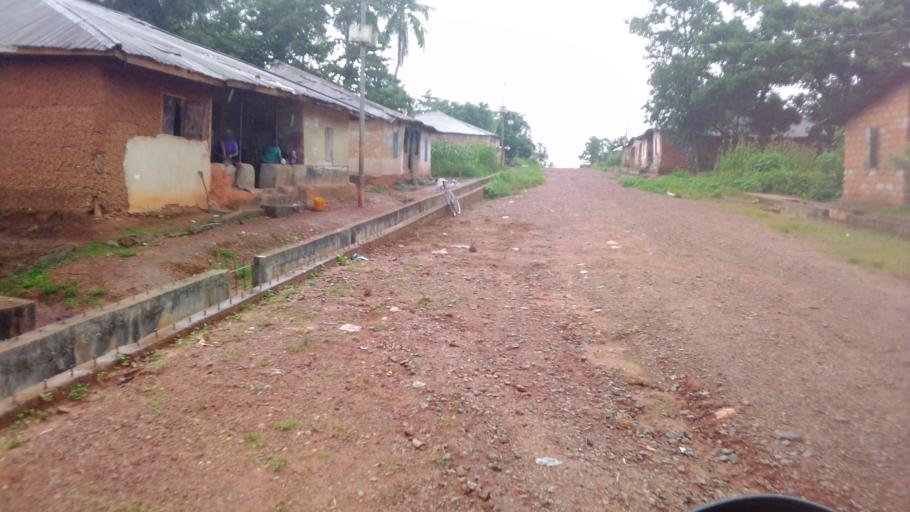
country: SL
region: Northern Province
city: Lunsar
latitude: 8.6821
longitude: -12.5301
